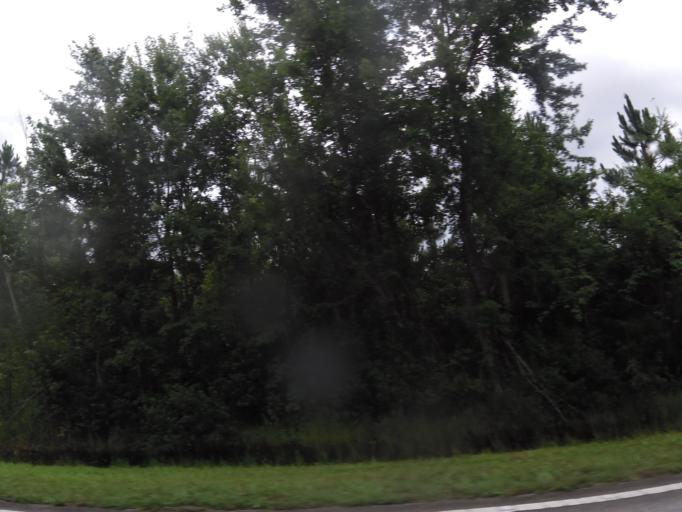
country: US
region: Florida
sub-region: Saint Johns County
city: Saint Augustine South
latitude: 29.8566
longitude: -81.4458
